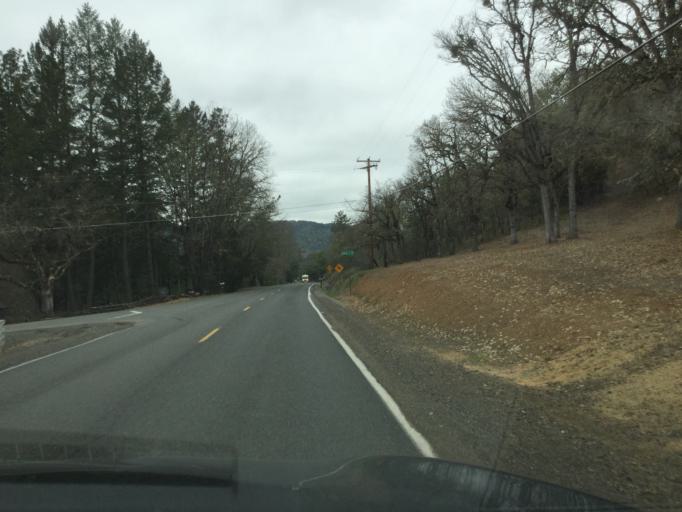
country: US
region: Oregon
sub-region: Jackson County
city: Gold Hill
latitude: 42.4004
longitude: -123.0223
